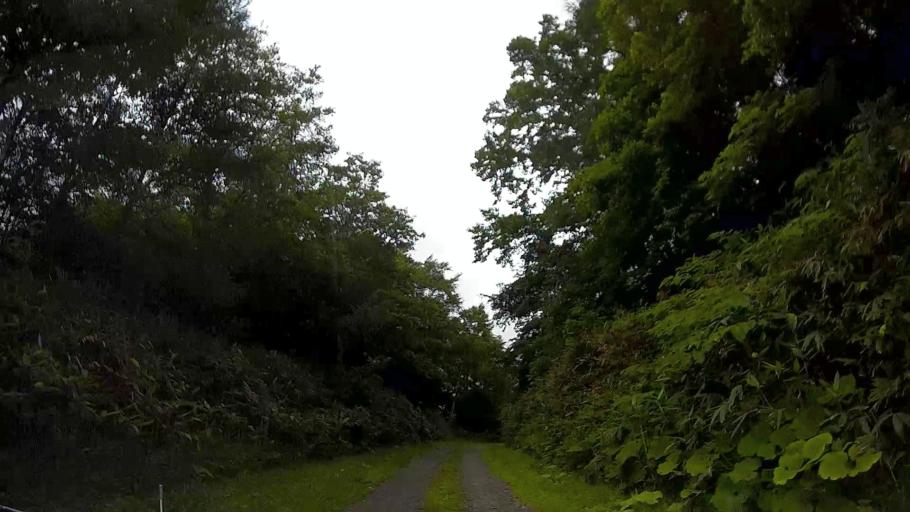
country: JP
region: Hokkaido
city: Nanae
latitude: 42.0383
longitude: 140.4835
